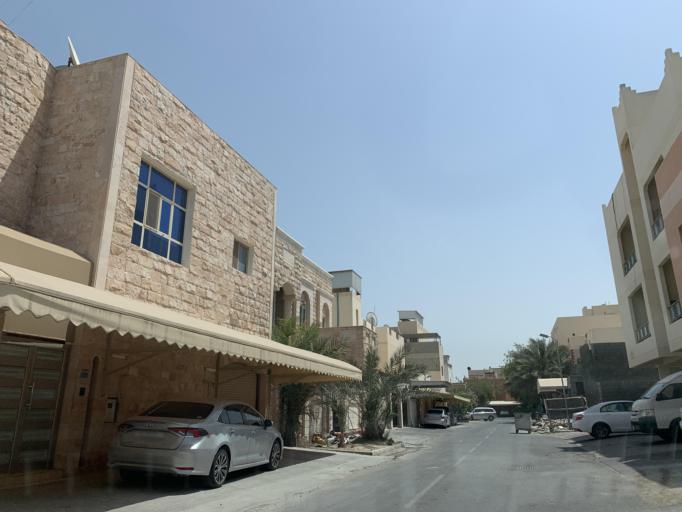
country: BH
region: Northern
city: Madinat `Isa
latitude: 26.1904
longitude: 50.5465
